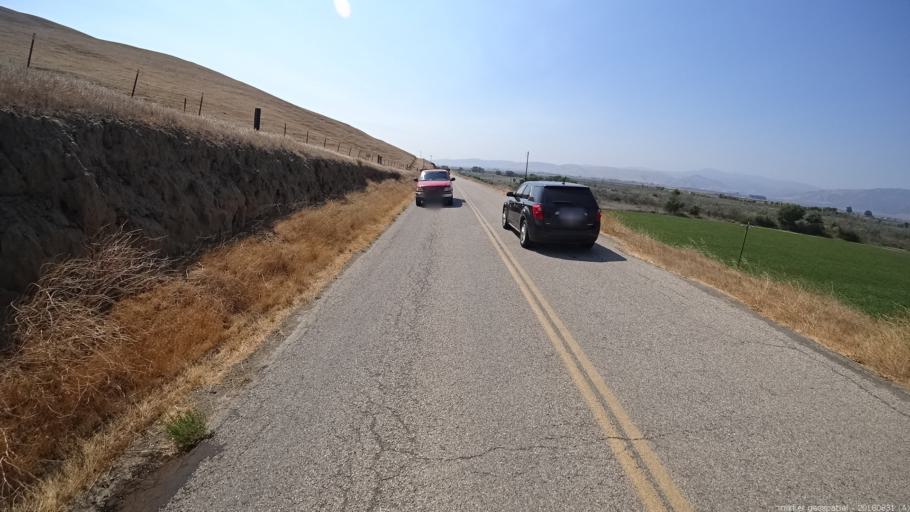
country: US
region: California
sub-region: Monterey County
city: Greenfield
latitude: 36.3760
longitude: -121.2398
